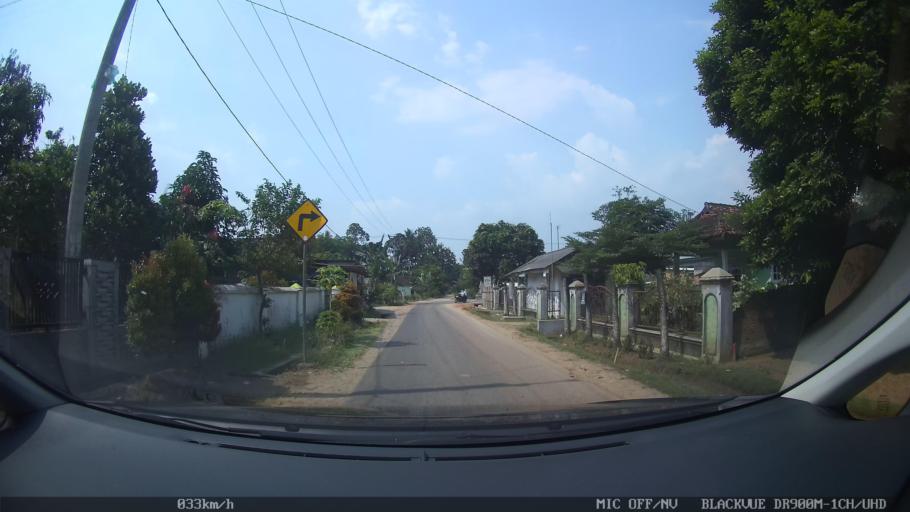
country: ID
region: Lampung
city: Natar
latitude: -5.2954
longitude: 105.2448
